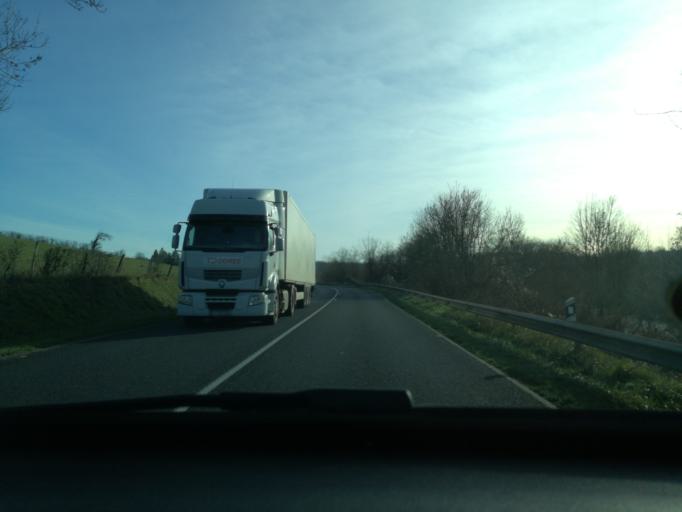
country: FR
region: Lorraine
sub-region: Departement de la Meuse
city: Fains-Veel
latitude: 48.8051
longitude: 5.1148
